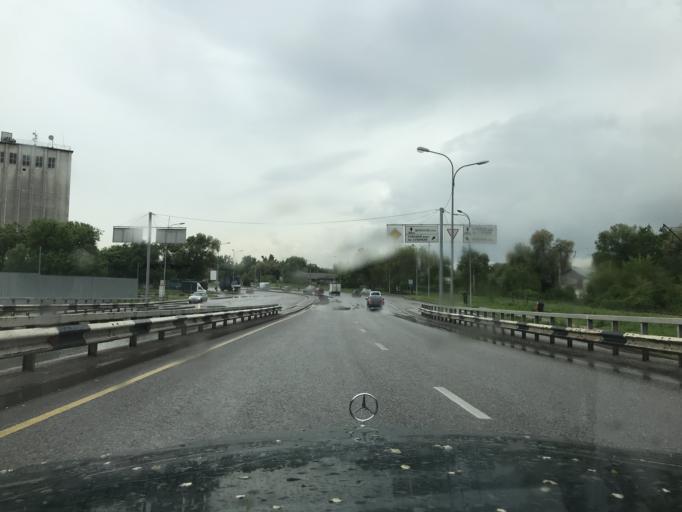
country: KZ
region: Almaty Oblysy
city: Pervomayskiy
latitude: 43.3344
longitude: 76.9621
